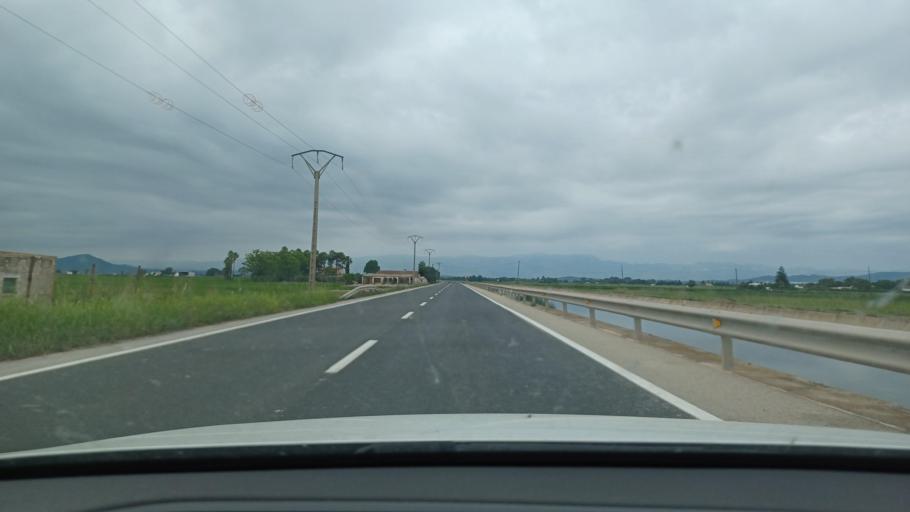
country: ES
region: Catalonia
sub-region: Provincia de Tarragona
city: Deltebre
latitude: 40.7102
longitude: 0.6815
